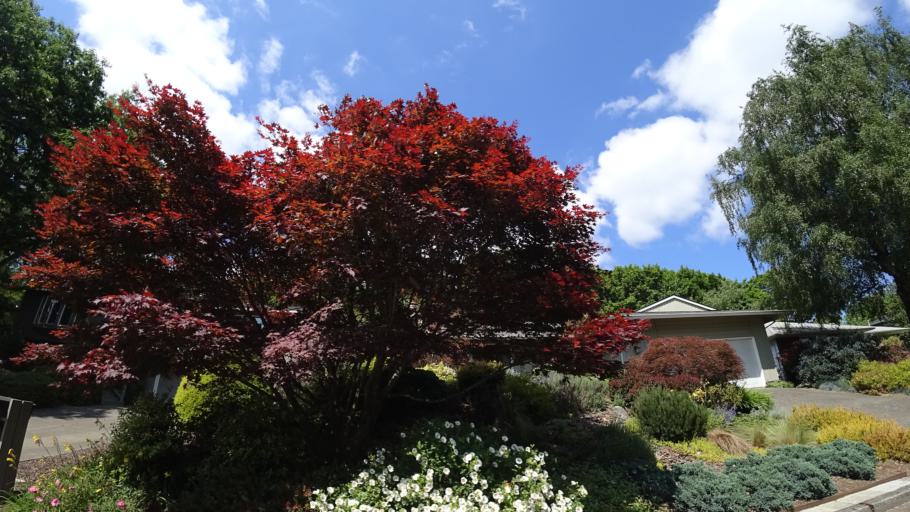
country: US
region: Oregon
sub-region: Clackamas County
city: Lake Oswego
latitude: 45.4692
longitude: -122.7010
